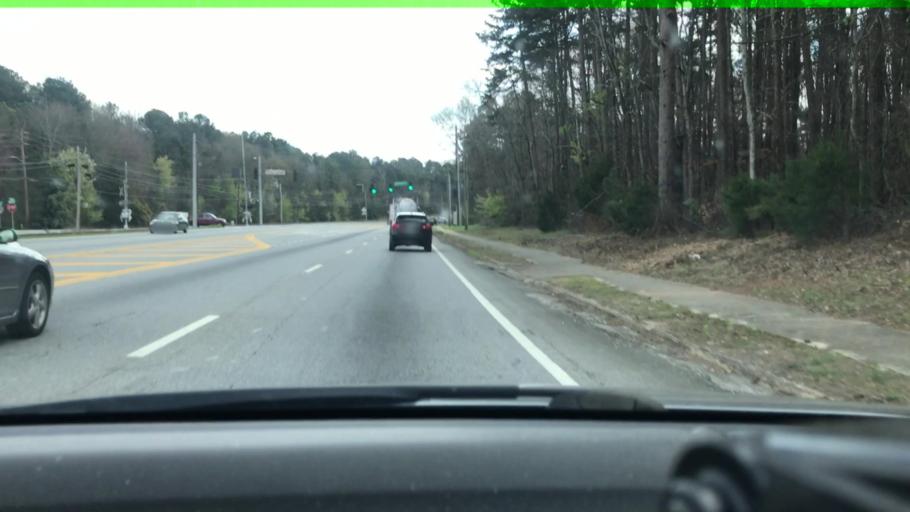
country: US
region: Georgia
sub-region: Clarke County
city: Country Club Estates
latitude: 33.9835
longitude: -83.4176
